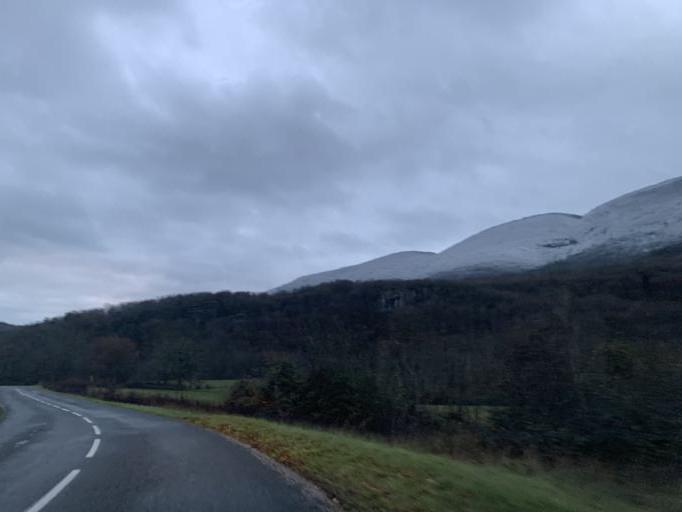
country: FR
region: Rhone-Alpes
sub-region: Departement de l'Ain
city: Virieu-le-Grand
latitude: 45.8181
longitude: 5.6116
